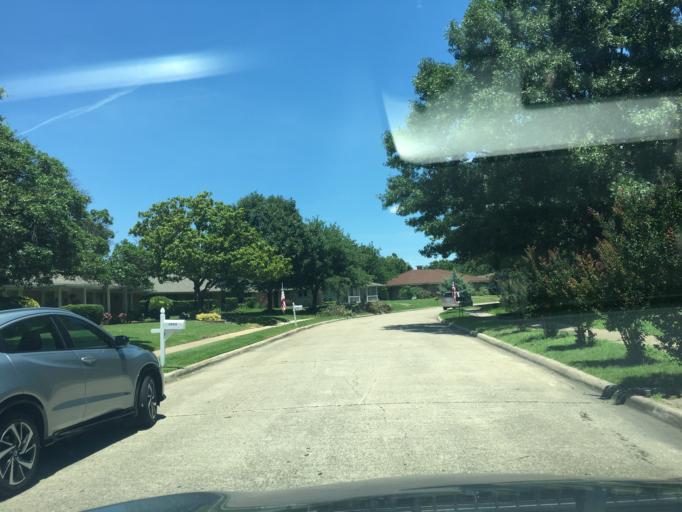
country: US
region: Texas
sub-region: Dallas County
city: Richardson
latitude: 32.9508
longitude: -96.6866
